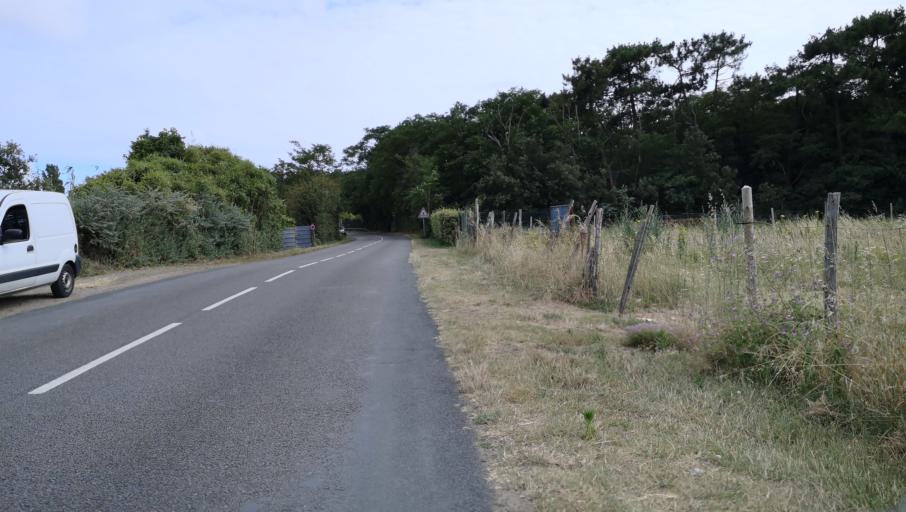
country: FR
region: Pays de la Loire
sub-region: Departement de la Vendee
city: Les Sables-d'Olonne
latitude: 46.5255
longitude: -1.8106
